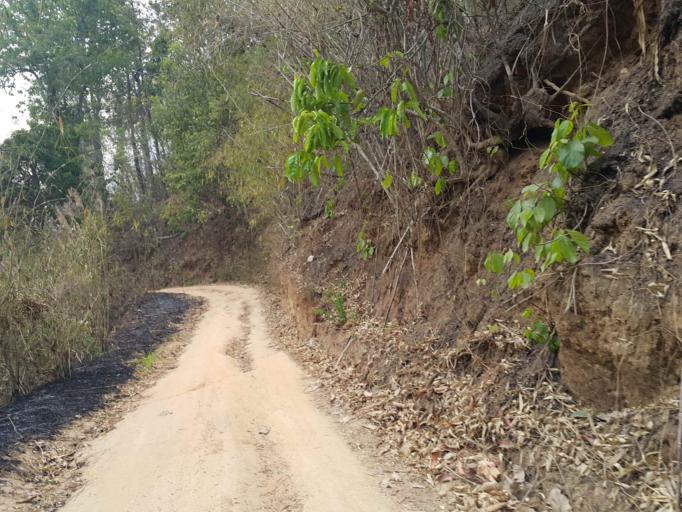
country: TH
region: Chiang Mai
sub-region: Amphoe Chiang Dao
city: Chiang Dao
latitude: 19.2812
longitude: 98.7640
